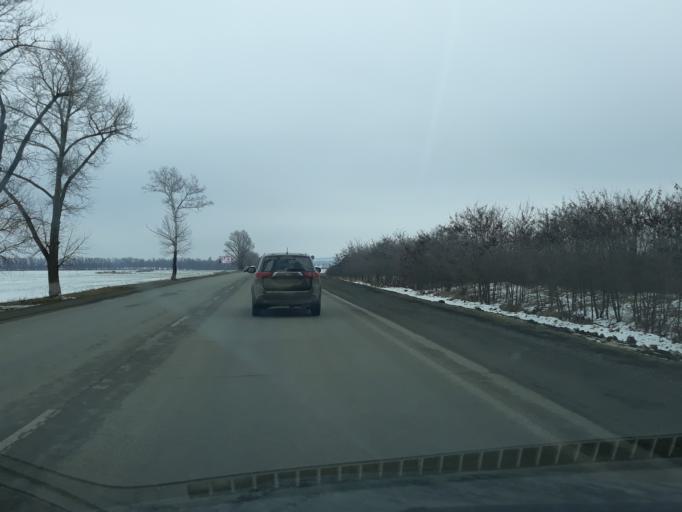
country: RU
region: Rostov
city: Primorka
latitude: 47.3058
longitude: 38.9935
